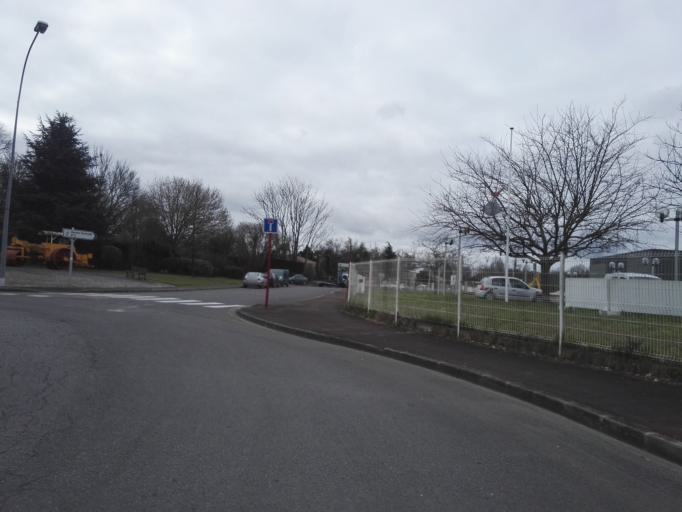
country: FR
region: Aquitaine
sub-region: Departement de la Gironde
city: Talence
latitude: 44.7827
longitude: -0.5769
